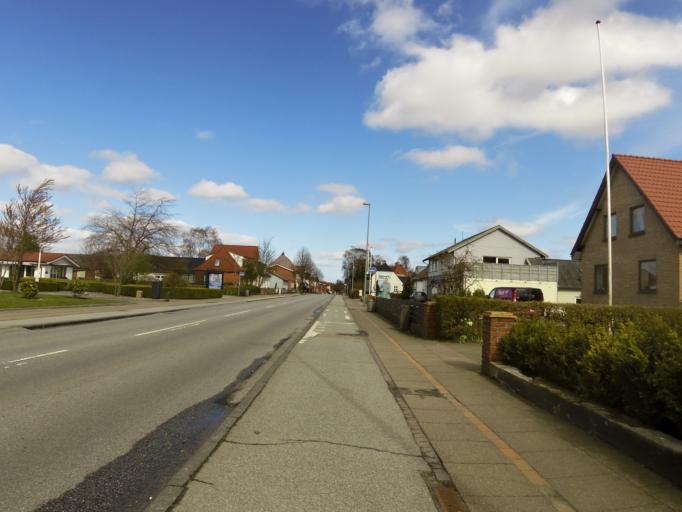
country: DK
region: South Denmark
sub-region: Haderslev Kommune
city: Vojens
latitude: 55.2449
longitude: 9.2938
